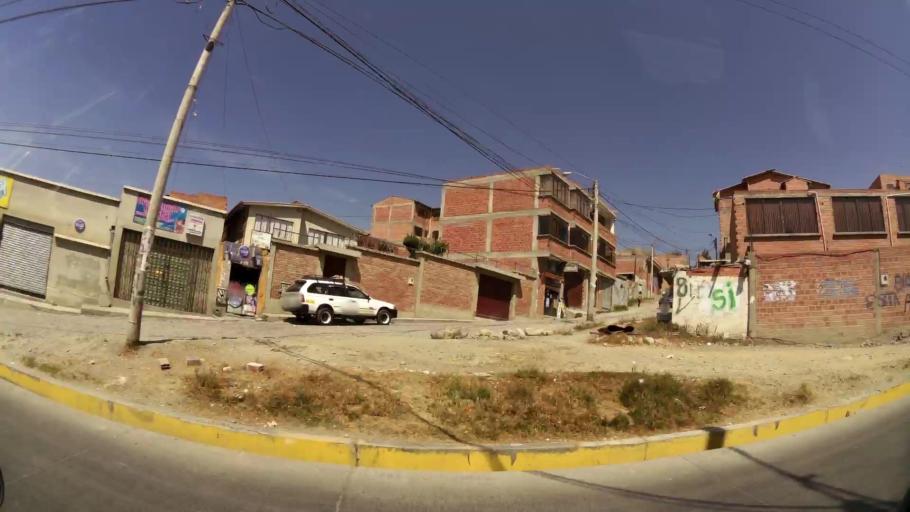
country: BO
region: La Paz
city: La Paz
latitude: -16.5286
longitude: -68.1241
